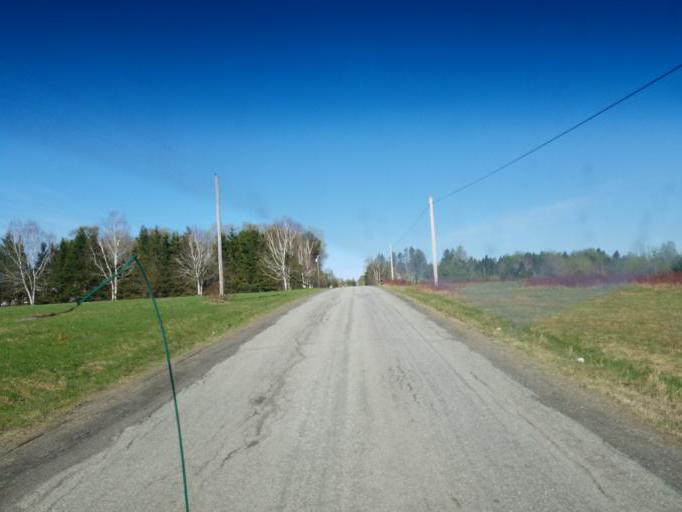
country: US
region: Maine
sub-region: Aroostook County
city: Caribou
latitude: 46.8441
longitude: -68.2086
